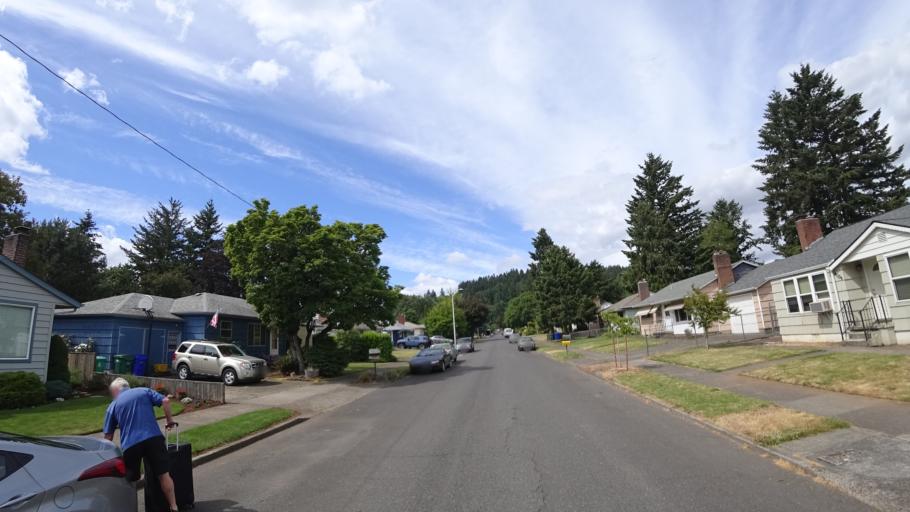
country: US
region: Oregon
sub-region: Multnomah County
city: Lents
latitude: 45.4926
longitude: -122.5583
